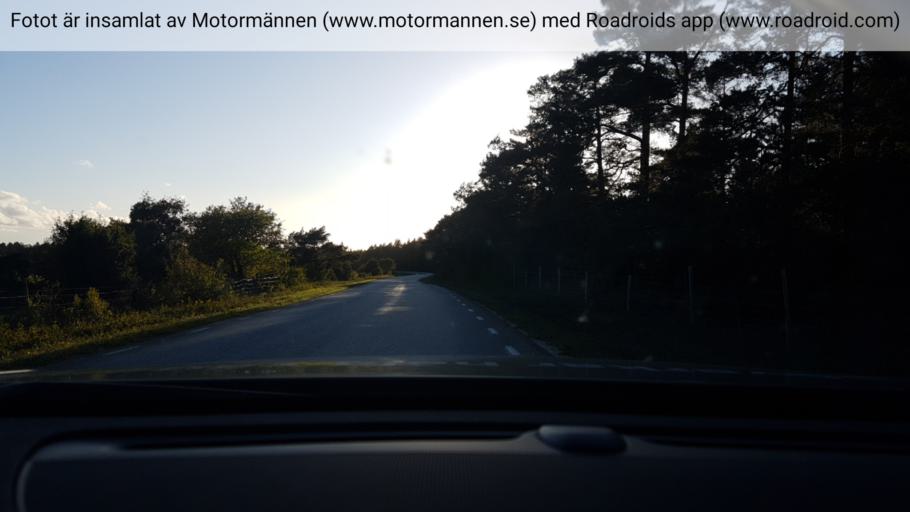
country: SE
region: Gotland
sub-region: Gotland
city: Slite
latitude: 57.8478
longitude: 18.6515
